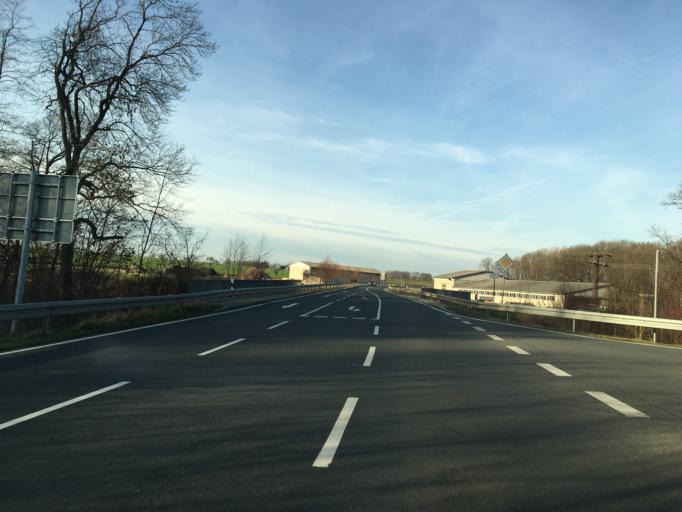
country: DE
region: Saxony
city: Naundorf
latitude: 51.2743
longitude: 13.1420
